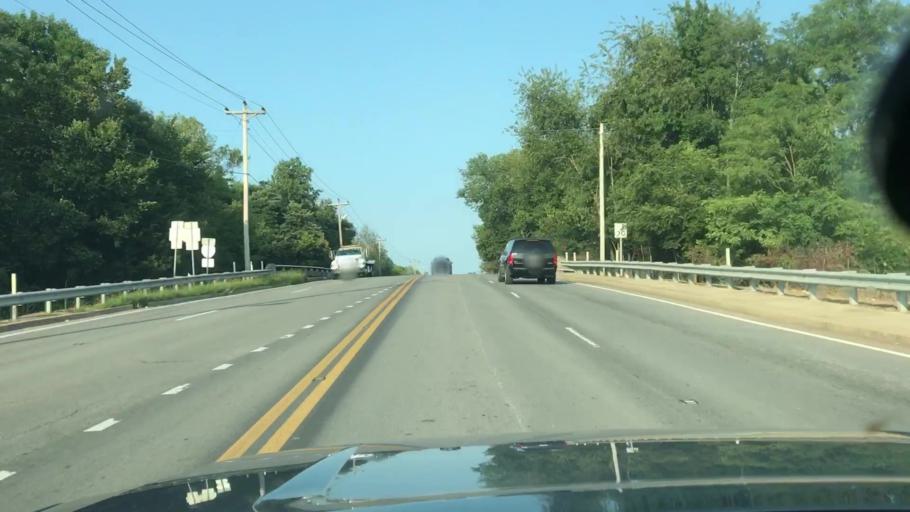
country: US
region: Tennessee
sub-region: Sumner County
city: Portland
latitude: 36.5770
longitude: -86.5133
